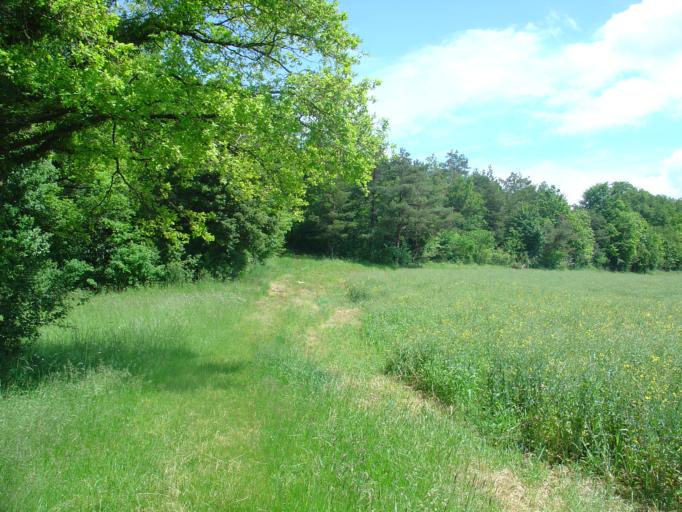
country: FR
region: Lorraine
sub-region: Departement de Meurthe-et-Moselle
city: Montauville
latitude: 48.8380
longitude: 5.9163
